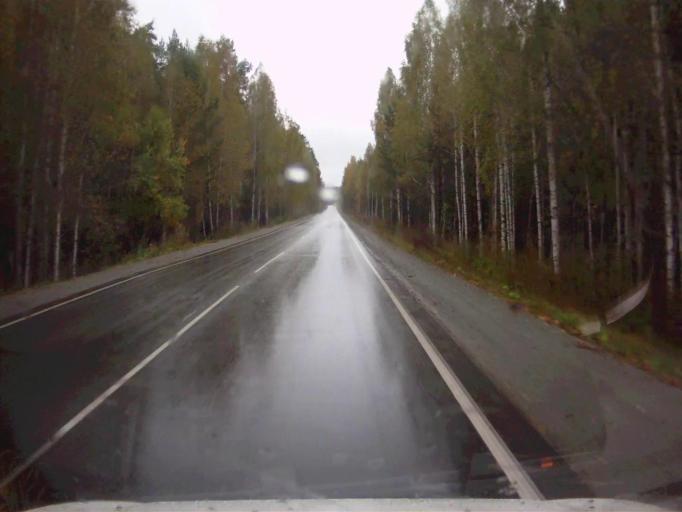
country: RU
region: Chelyabinsk
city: Kyshtym
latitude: 55.6476
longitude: 60.5837
